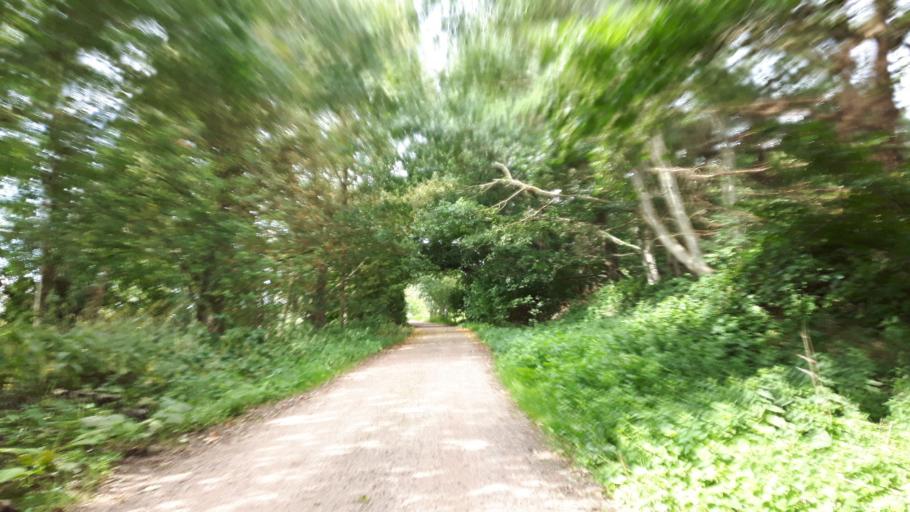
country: NL
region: Groningen
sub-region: Gemeente Leek
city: Leek
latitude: 53.0811
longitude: 6.3351
